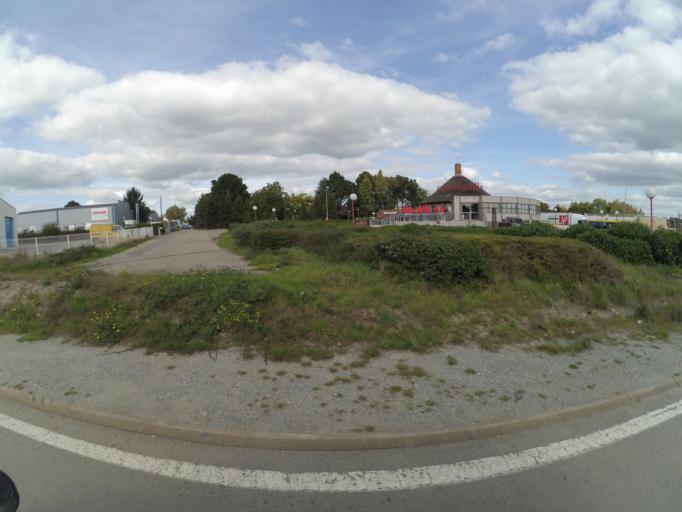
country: FR
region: Pays de la Loire
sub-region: Departement de la Loire-Atlantique
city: Thouare-sur-Loire
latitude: 47.2827
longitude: -1.4546
